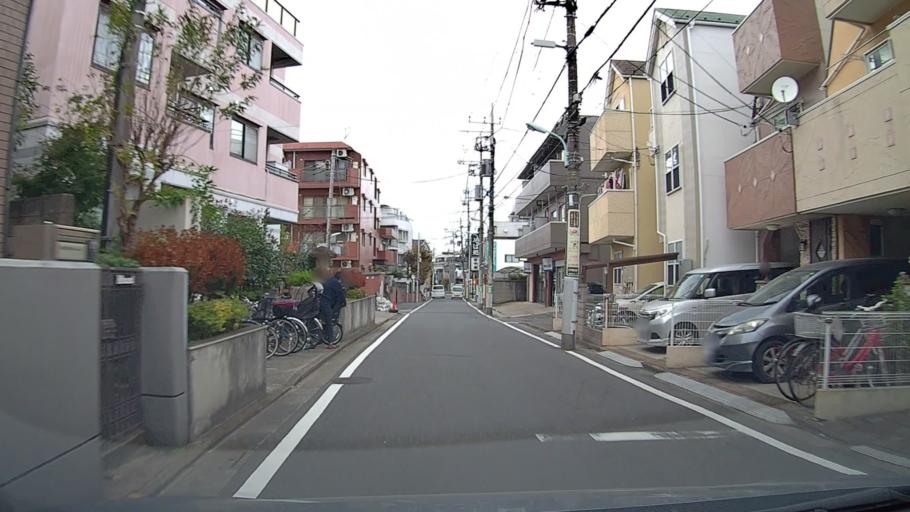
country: JP
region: Saitama
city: Wako
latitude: 35.7317
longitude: 139.6132
